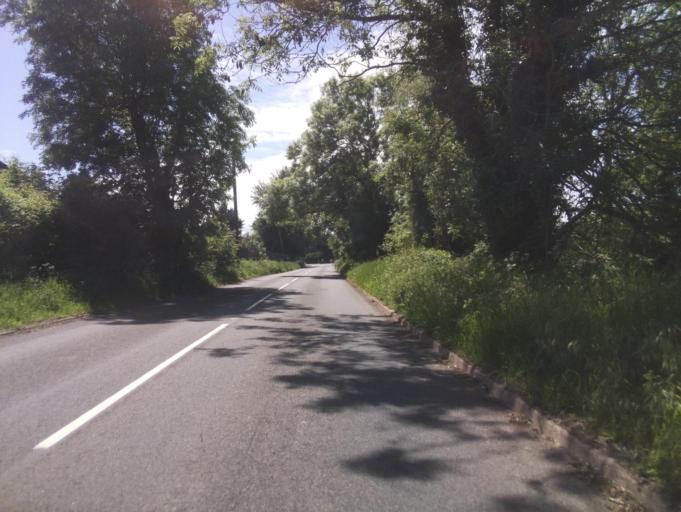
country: GB
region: Wales
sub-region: Monmouthshire
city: Caldicot
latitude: 51.6104
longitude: -2.7381
